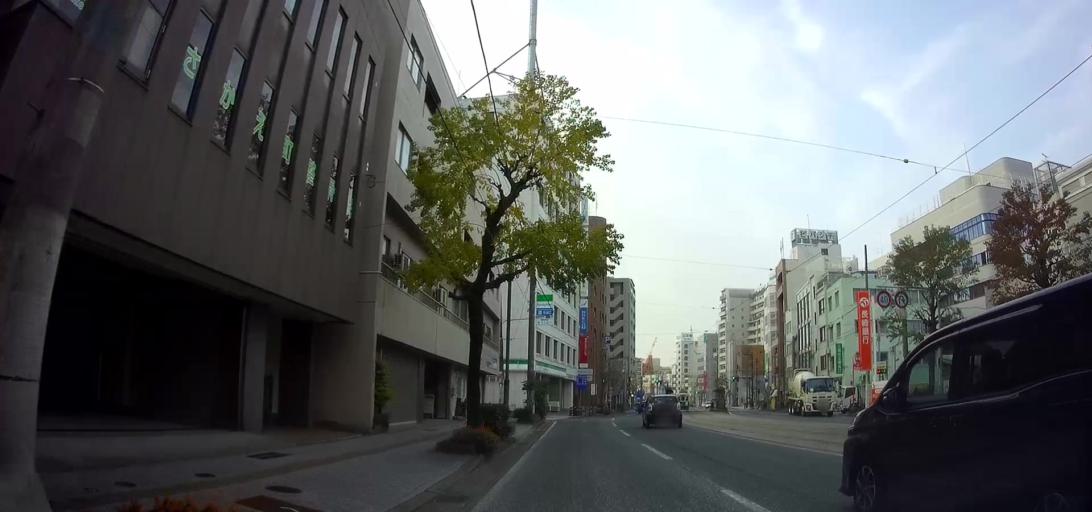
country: JP
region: Nagasaki
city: Nagasaki-shi
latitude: 32.7478
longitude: 129.8797
